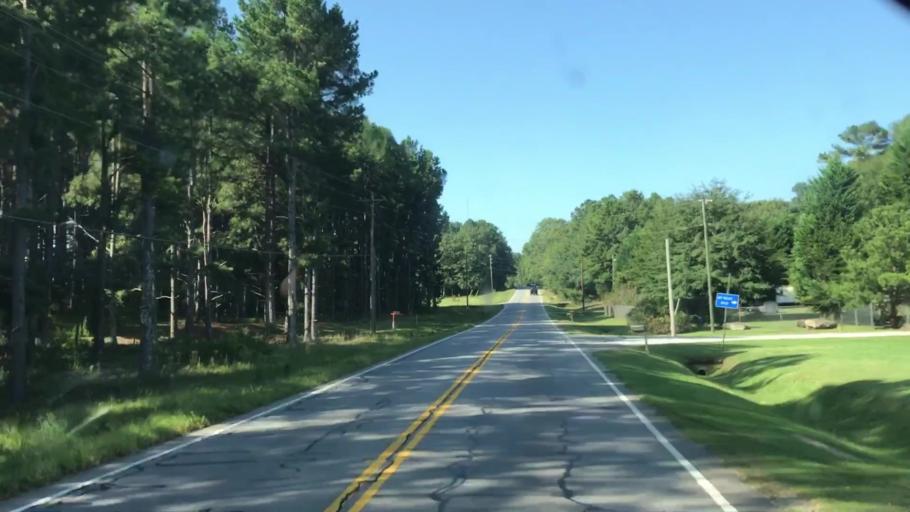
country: US
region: Georgia
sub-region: Walton County
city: Loganville
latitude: 33.8932
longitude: -83.8066
